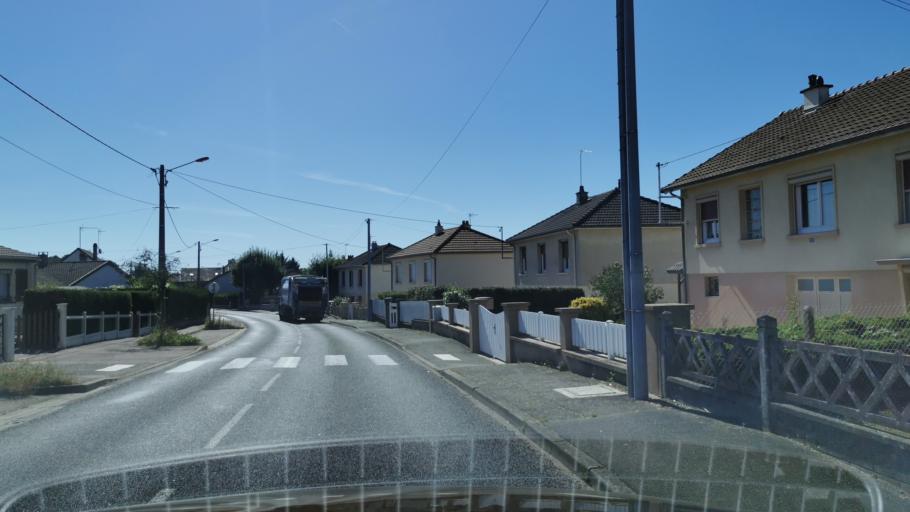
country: FR
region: Bourgogne
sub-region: Departement de Saone-et-Loire
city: Le Breuil
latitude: 46.8036
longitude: 4.4686
